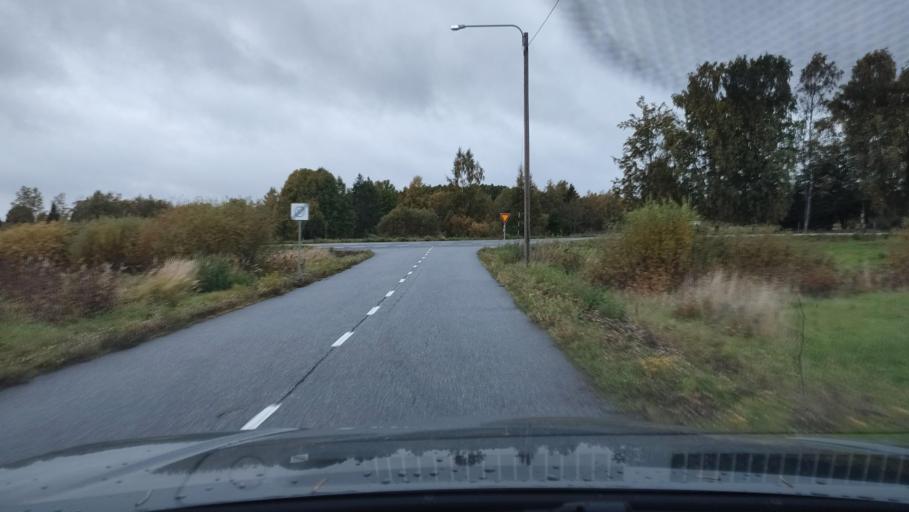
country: FI
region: Ostrobothnia
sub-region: Sydosterbotten
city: Kristinestad
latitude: 62.2797
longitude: 21.4073
